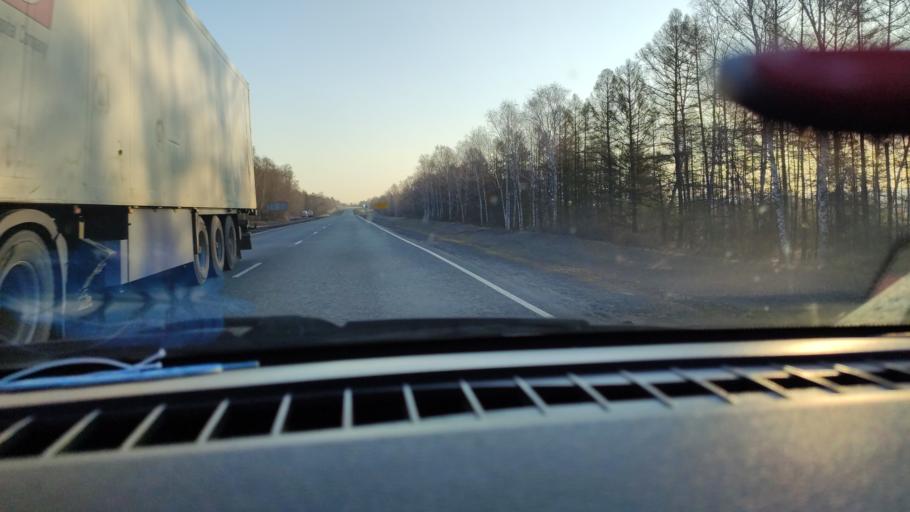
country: RU
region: Saratov
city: Sennoy
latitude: 52.1274
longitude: 46.8561
